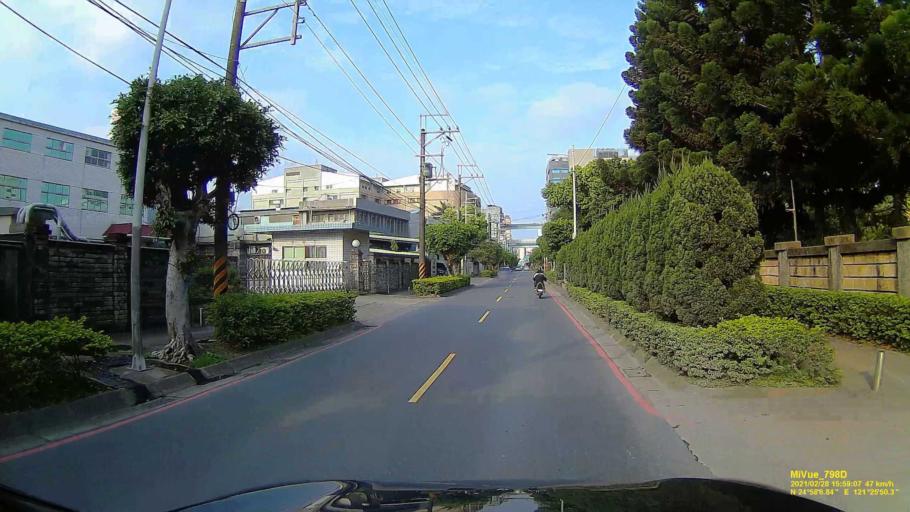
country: TW
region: Taipei
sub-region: Taipei
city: Banqiao
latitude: 24.9688
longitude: 121.4309
